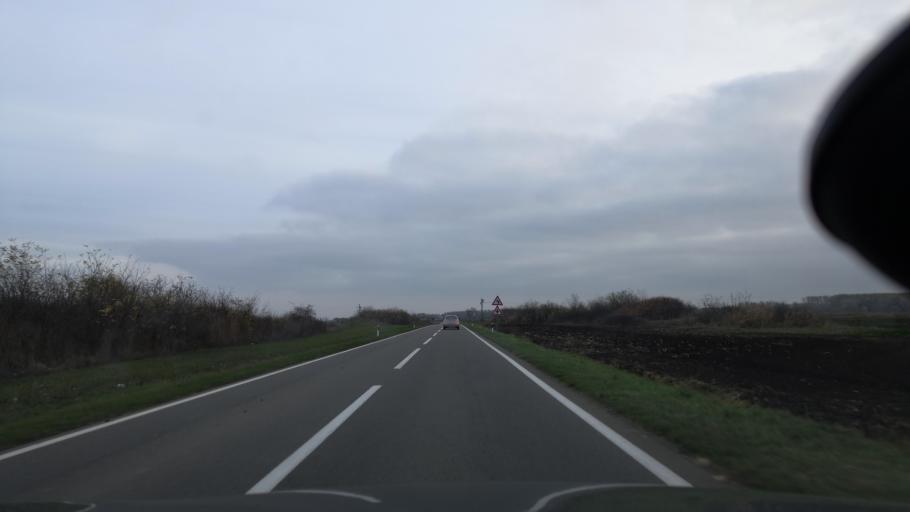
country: RS
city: Sanad
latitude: 46.0021
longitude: 20.1020
